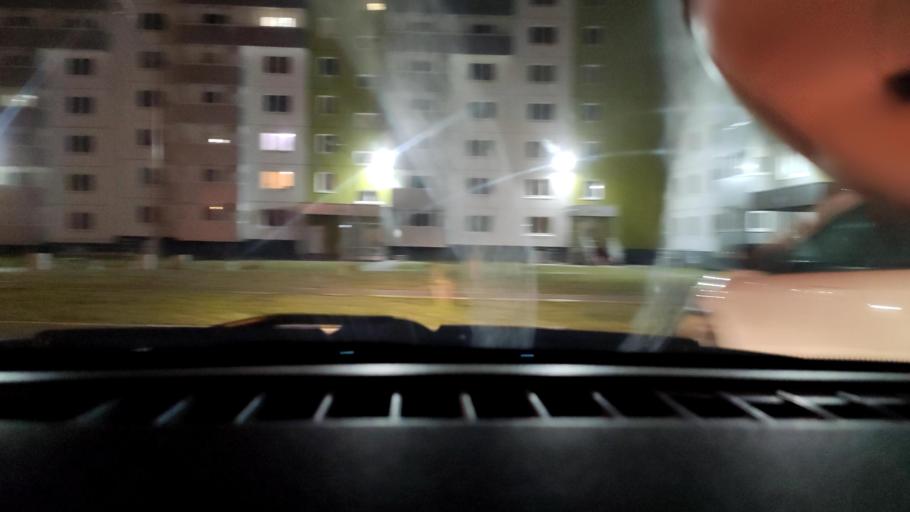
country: RU
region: Perm
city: Kondratovo
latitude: 57.9895
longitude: 56.1193
